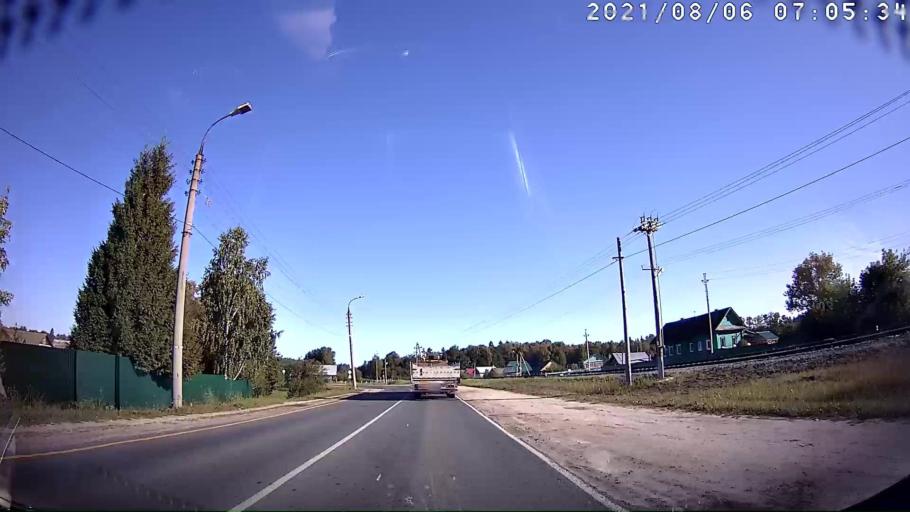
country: RU
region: Mariy-El
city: Yoshkar-Ola
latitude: 56.5543
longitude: 47.9864
